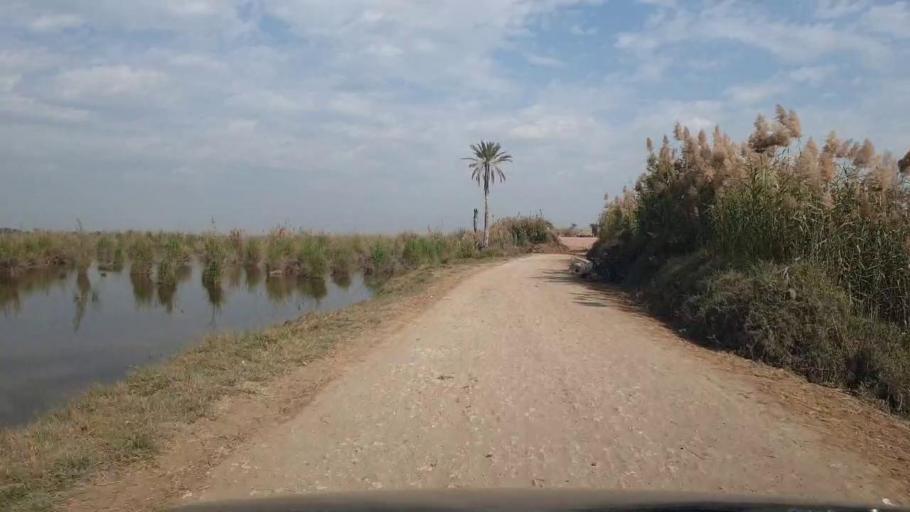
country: PK
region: Sindh
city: Hala
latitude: 25.9958
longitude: 68.4414
